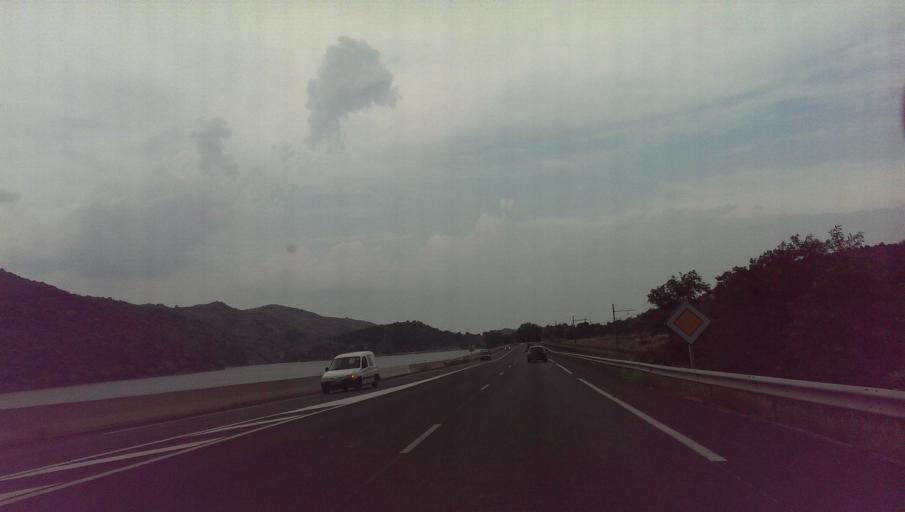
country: FR
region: Languedoc-Roussillon
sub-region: Departement des Pyrenees-Orientales
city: Vinca
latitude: 42.6500
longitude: 2.5314
